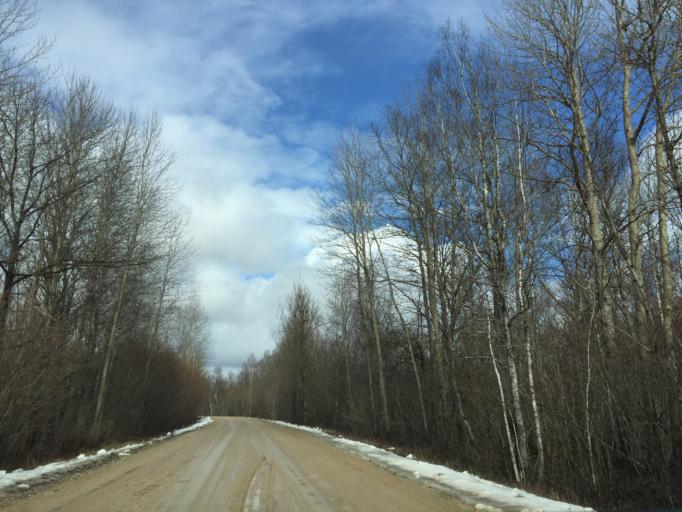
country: EE
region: Laeaene
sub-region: Lihula vald
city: Lihula
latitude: 58.7244
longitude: 23.8300
